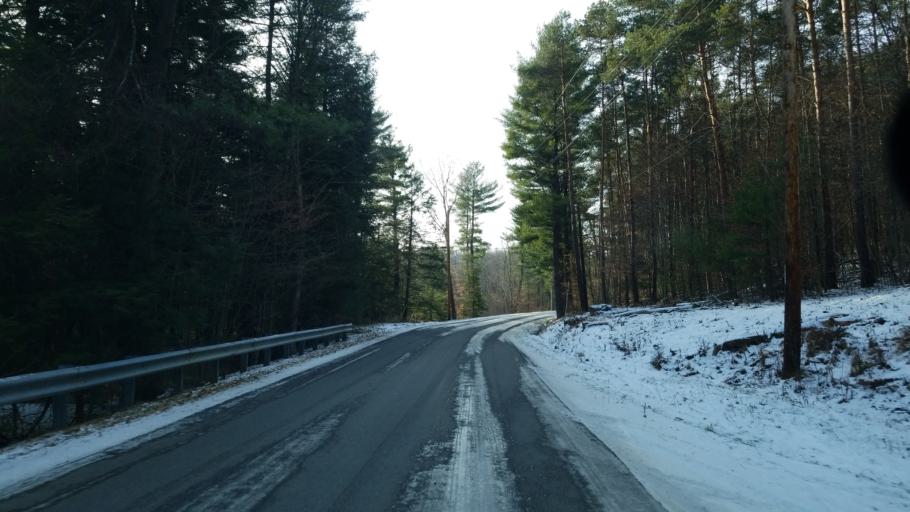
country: US
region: Pennsylvania
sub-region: Clearfield County
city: Treasure Lake
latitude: 41.1021
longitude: -78.6697
